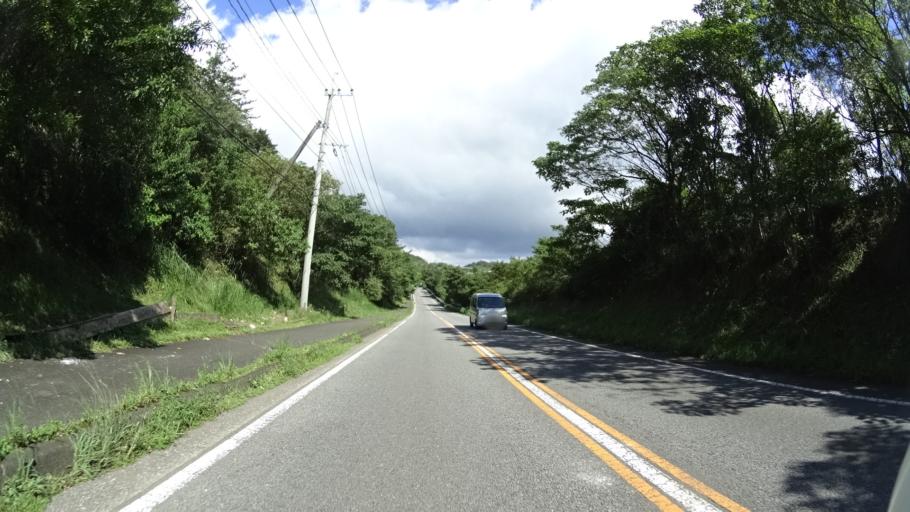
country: JP
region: Oita
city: Beppu
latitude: 33.3390
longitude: 131.4594
